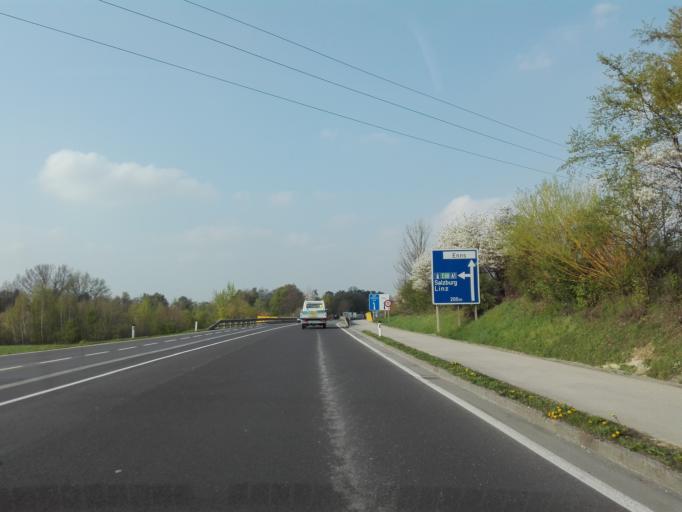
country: AT
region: Upper Austria
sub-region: Politischer Bezirk Linz-Land
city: Enns
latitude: 48.2013
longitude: 14.4748
